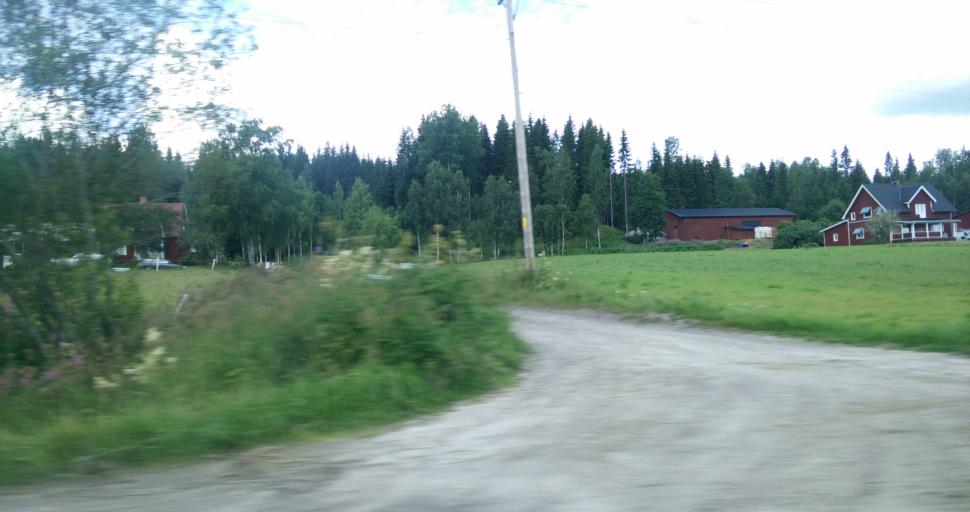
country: SE
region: Vaermland
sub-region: Hagfors Kommun
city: Ekshaerad
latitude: 60.1212
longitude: 13.4527
